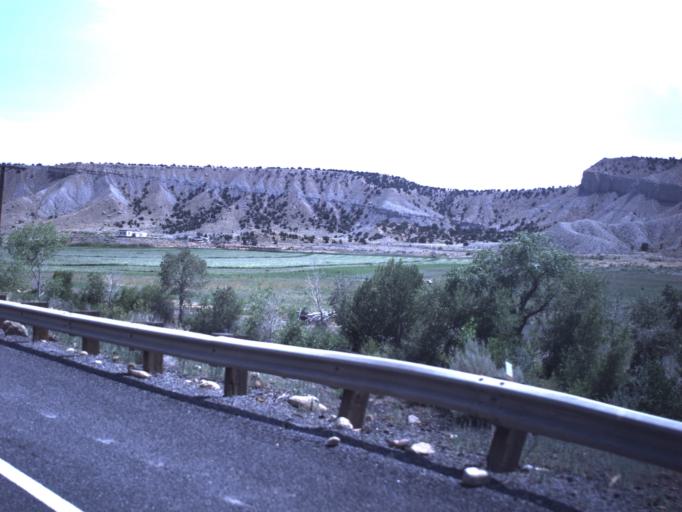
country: US
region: Utah
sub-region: Emery County
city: Huntington
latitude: 39.3556
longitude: -111.0269
